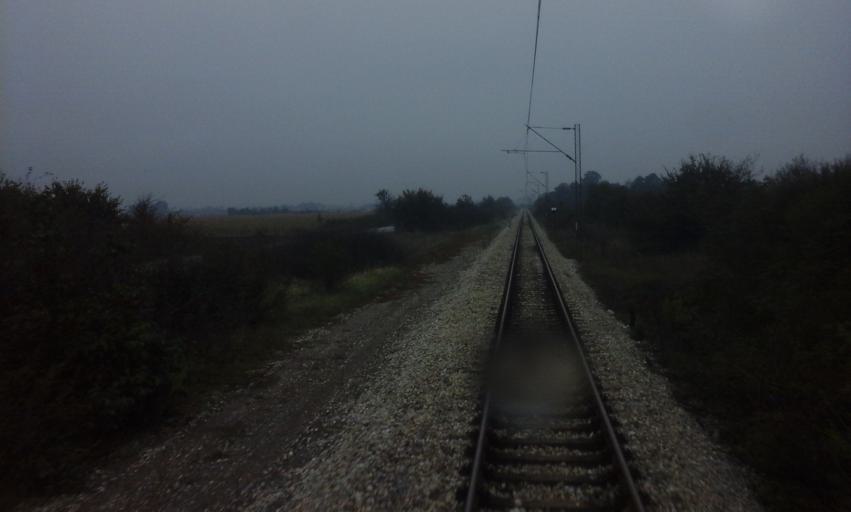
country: RS
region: Central Serbia
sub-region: Pomoravski Okrug
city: Cuprija
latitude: 43.8925
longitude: 21.3817
